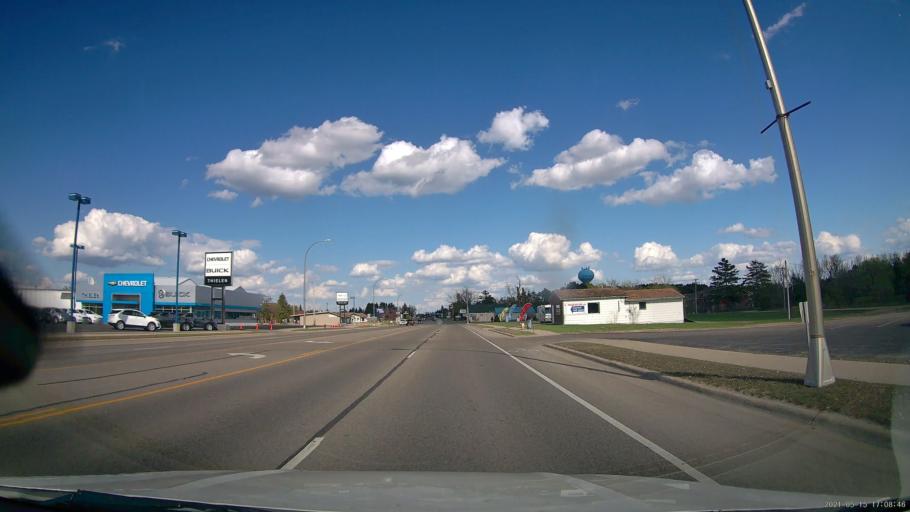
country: US
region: Minnesota
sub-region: Hubbard County
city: Park Rapids
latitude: 46.9220
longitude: -95.0442
